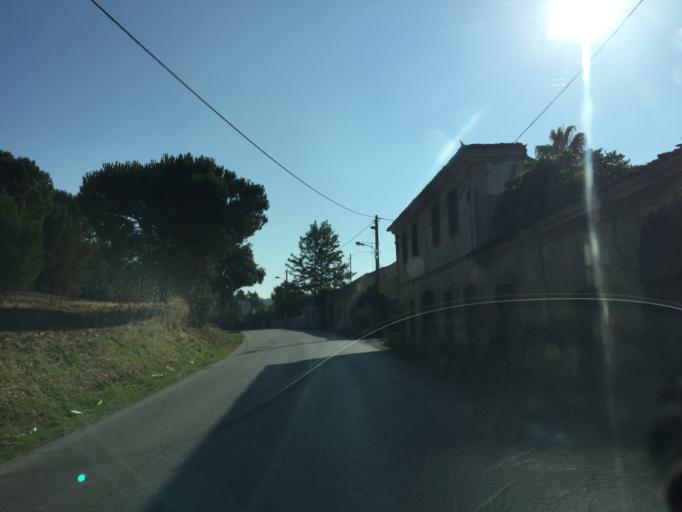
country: PT
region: Santarem
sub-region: Abrantes
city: Alferrarede
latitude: 39.4855
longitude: -8.1814
